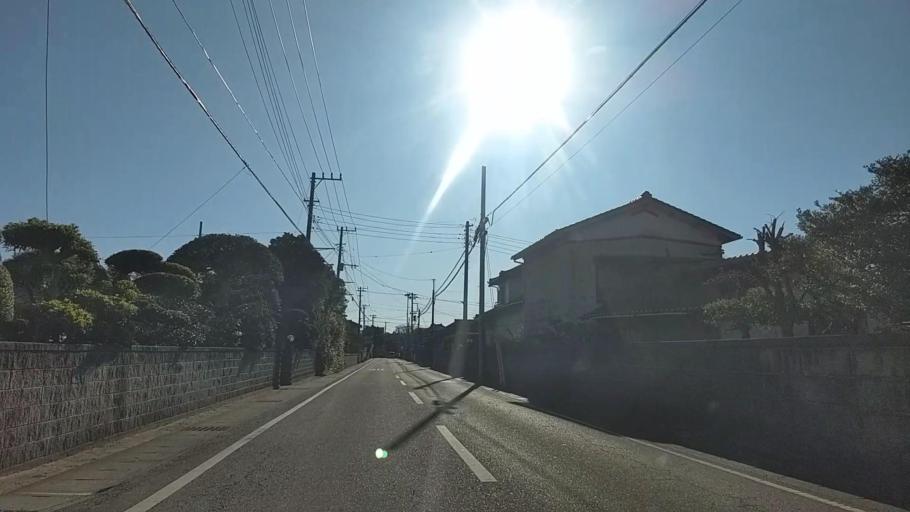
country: JP
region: Chiba
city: Futtsu
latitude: 35.3050
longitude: 139.8328
